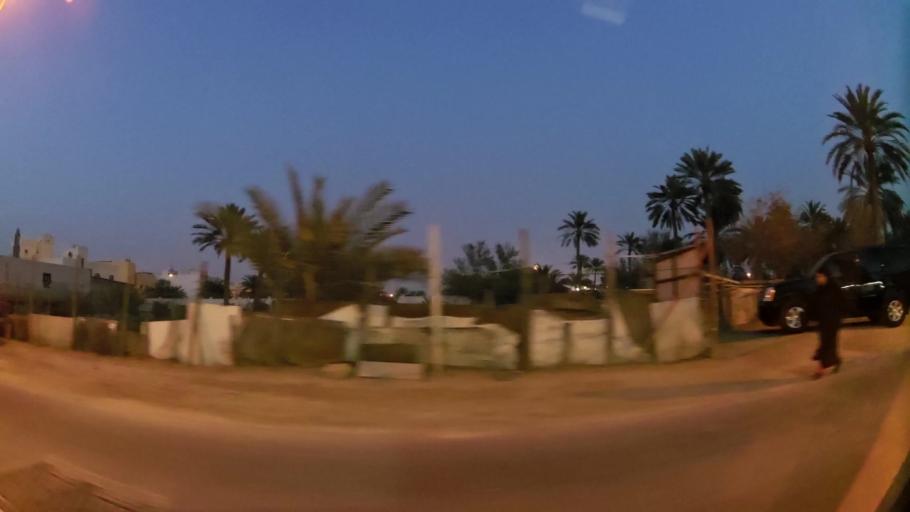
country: BH
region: Manama
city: Jidd Hafs
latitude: 26.2015
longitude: 50.5525
